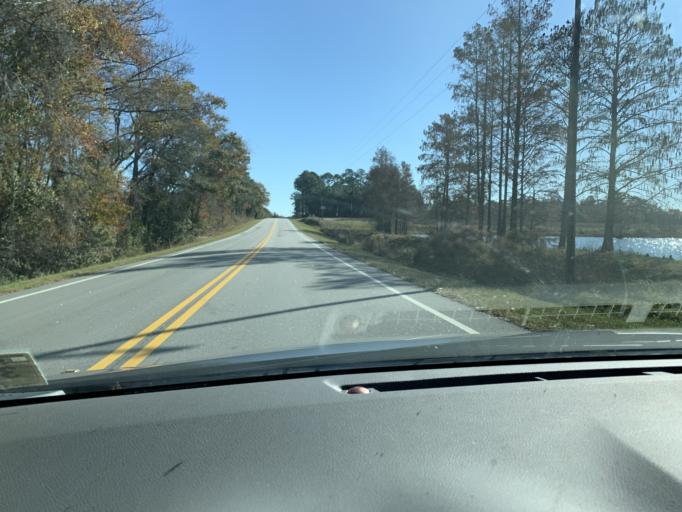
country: US
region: Georgia
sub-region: Ben Hill County
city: Fitzgerald
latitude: 31.7020
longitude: -83.1488
